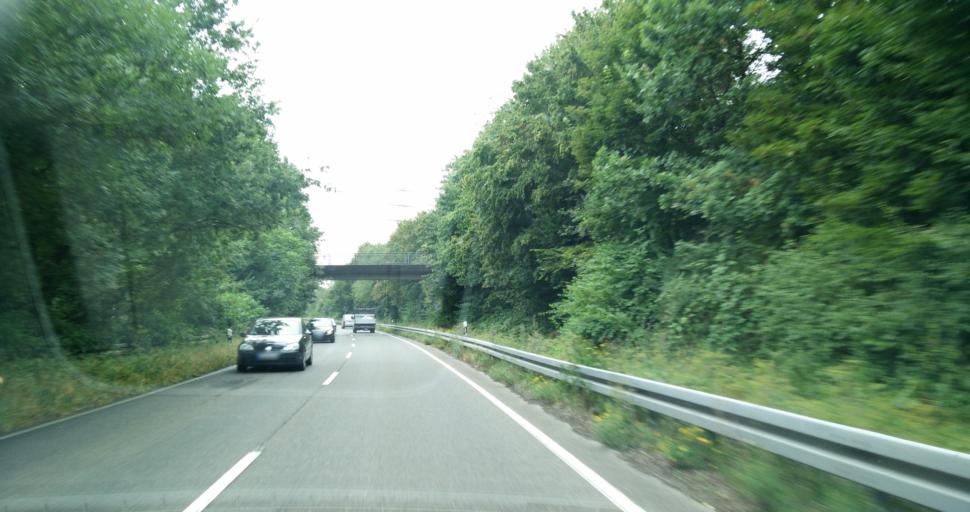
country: DE
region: North Rhine-Westphalia
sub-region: Regierungsbezirk Dusseldorf
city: Mettmann
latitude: 51.2680
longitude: 6.9354
